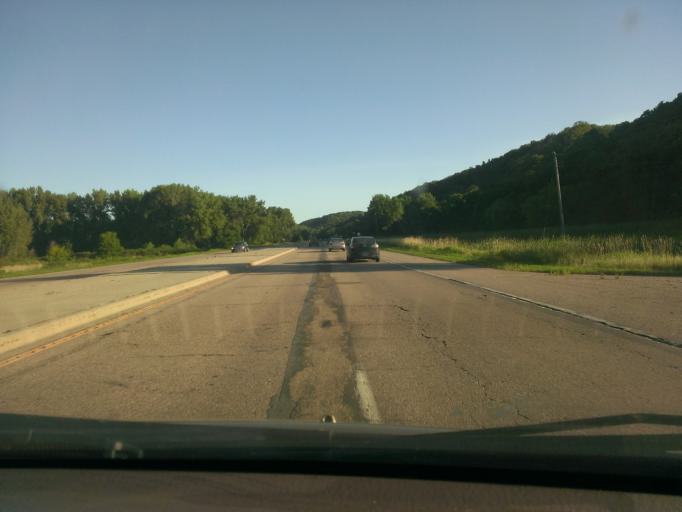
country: US
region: Minnesota
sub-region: Nicollet County
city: North Mankato
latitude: 44.2272
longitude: -94.0274
